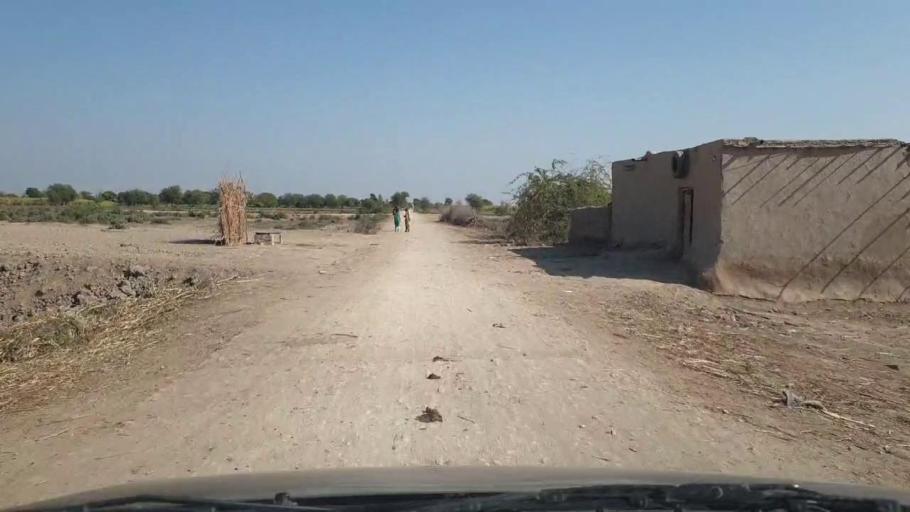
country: PK
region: Sindh
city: Samaro
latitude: 25.1997
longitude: 69.2659
